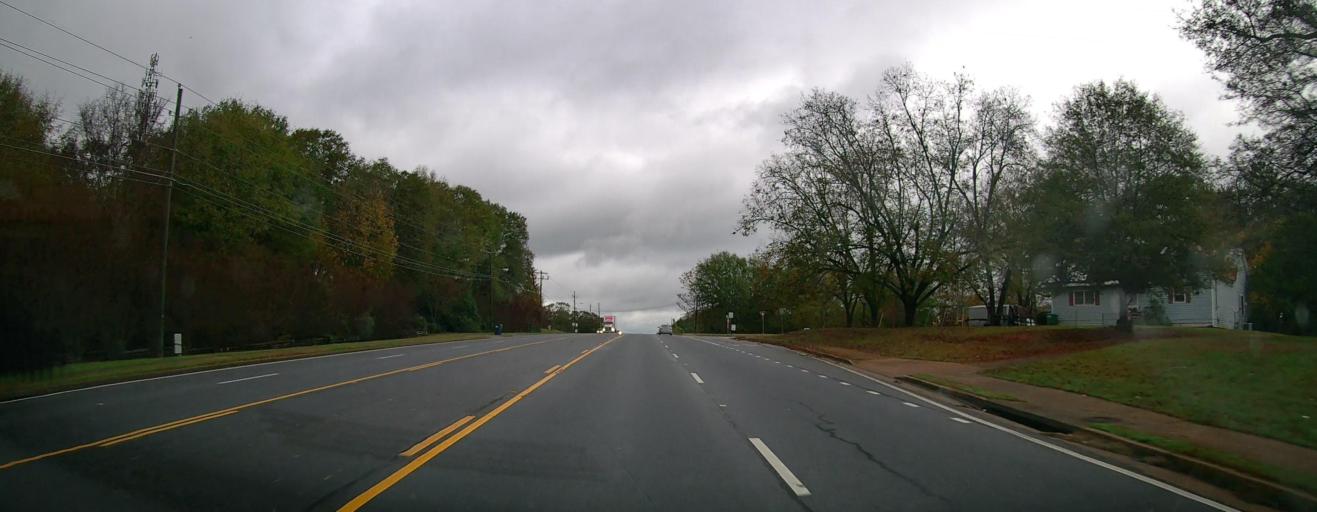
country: US
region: Georgia
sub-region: Jackson County
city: Nicholson
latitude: 34.1170
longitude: -83.4322
